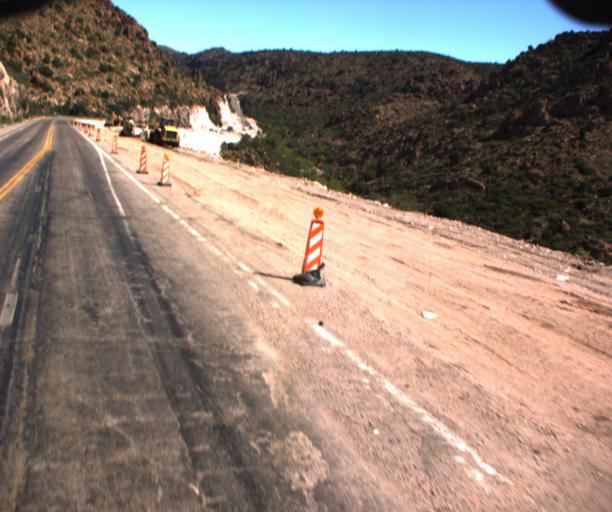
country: US
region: Arizona
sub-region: Pinal County
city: Superior
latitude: 33.3184
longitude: -111.0354
